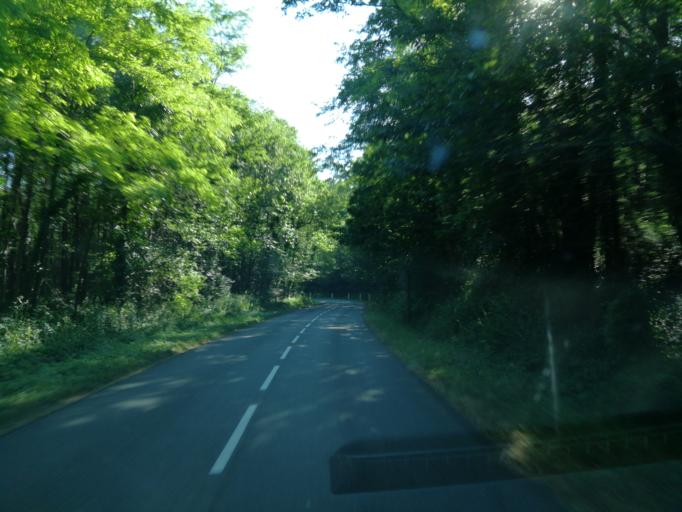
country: FR
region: Midi-Pyrenees
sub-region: Departement du Lot
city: Prayssac
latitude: 44.5986
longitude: 1.1907
